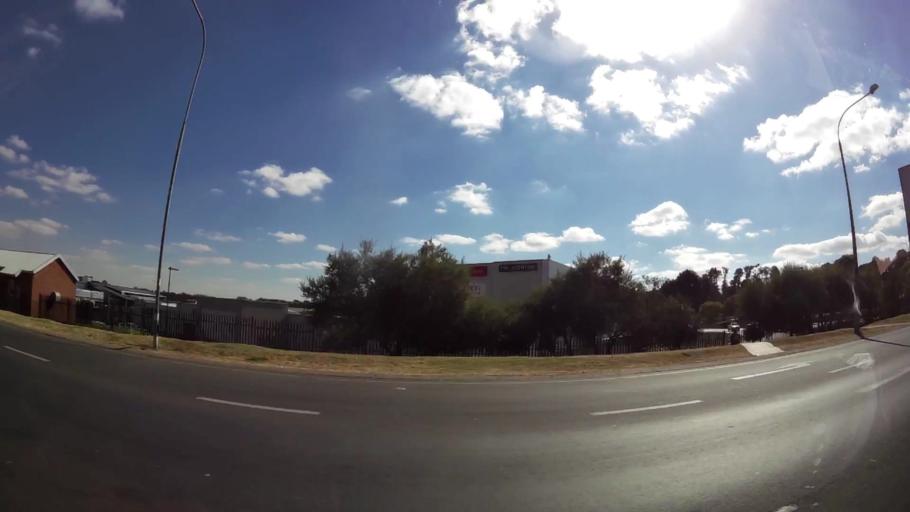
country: ZA
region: Gauteng
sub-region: West Rand District Municipality
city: Krugersdorp
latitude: -26.0882
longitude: 27.7841
